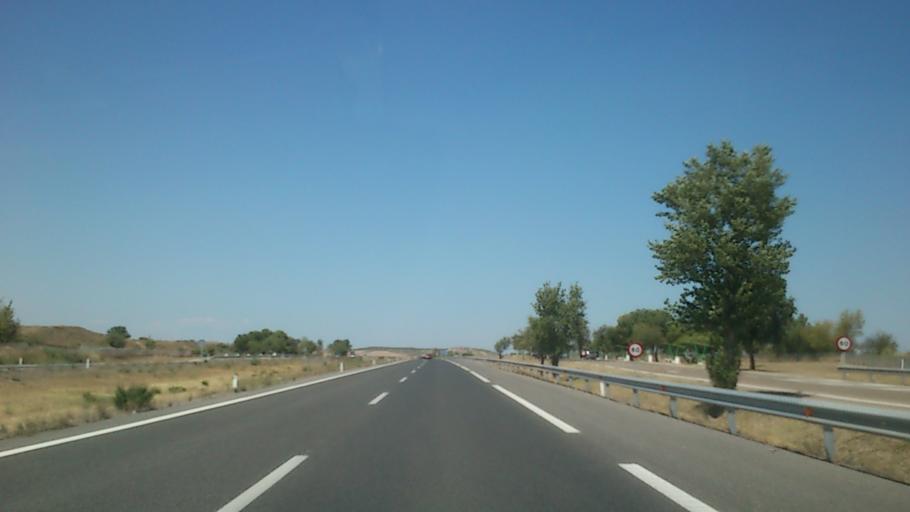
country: ES
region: Aragon
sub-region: Provincia de Zaragoza
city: Frescano
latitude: 41.9093
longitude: -1.4575
